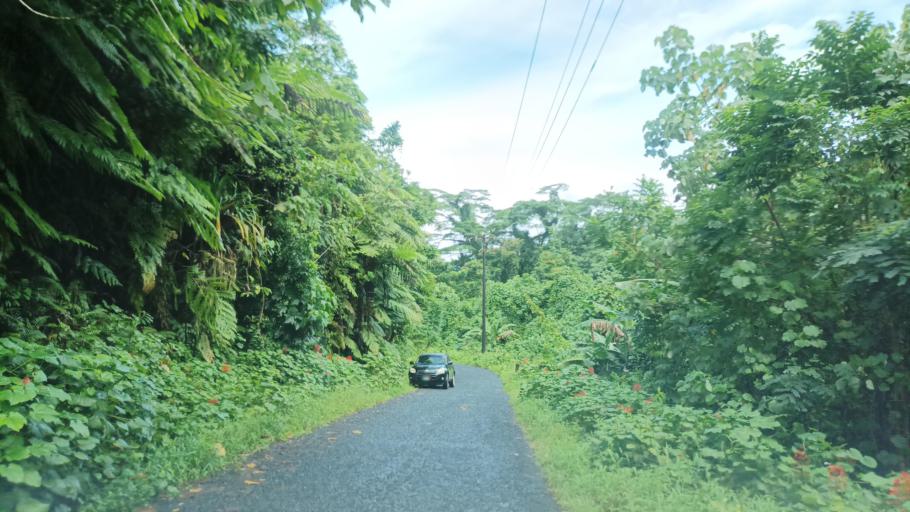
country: FM
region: Pohnpei
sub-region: Sokehs Municipality
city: Palikir - National Government Center
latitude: 6.9345
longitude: 158.1875
